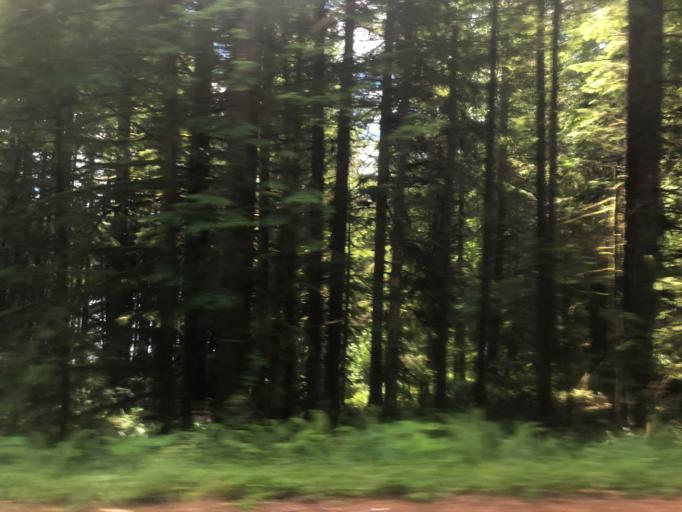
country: US
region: Oregon
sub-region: Clackamas County
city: Mount Hood Village
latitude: 45.4863
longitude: -122.0798
